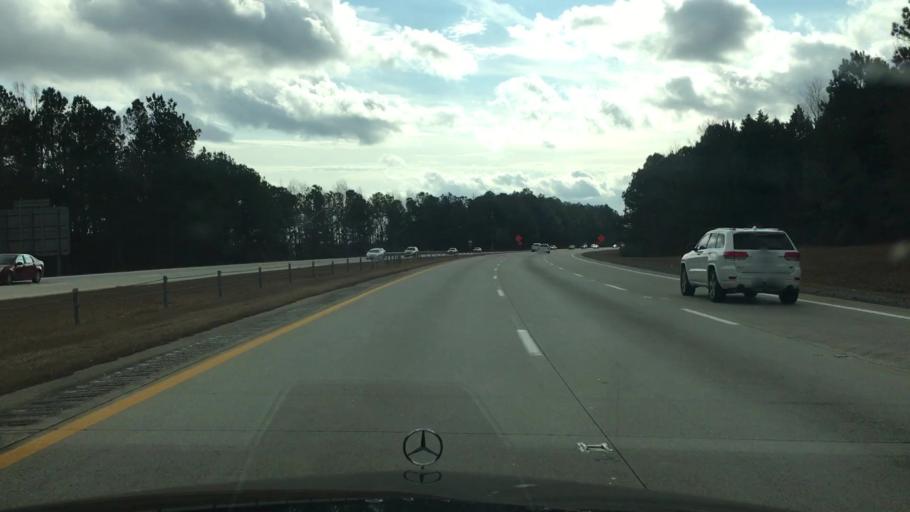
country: US
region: North Carolina
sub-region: Johnston County
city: Clayton
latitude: 35.6026
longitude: -78.5635
